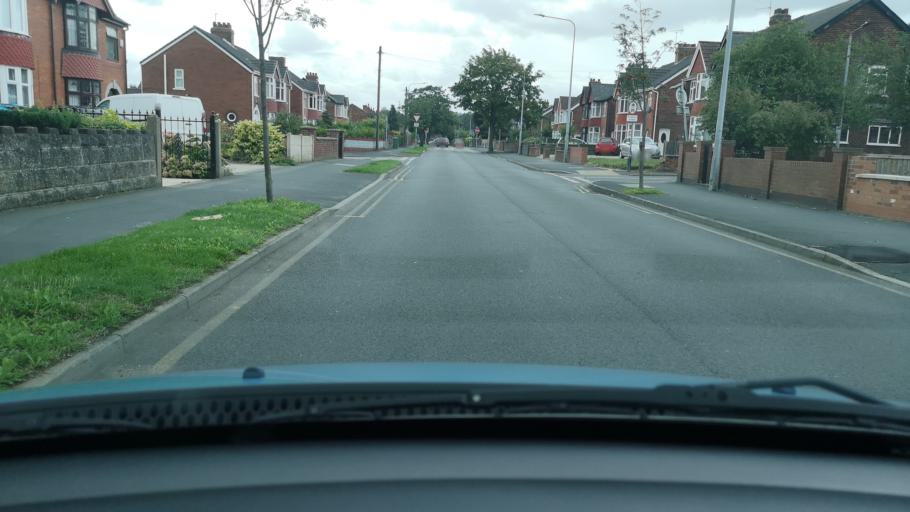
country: GB
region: England
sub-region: North Lincolnshire
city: Scunthorpe
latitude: 53.5893
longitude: -0.6610
